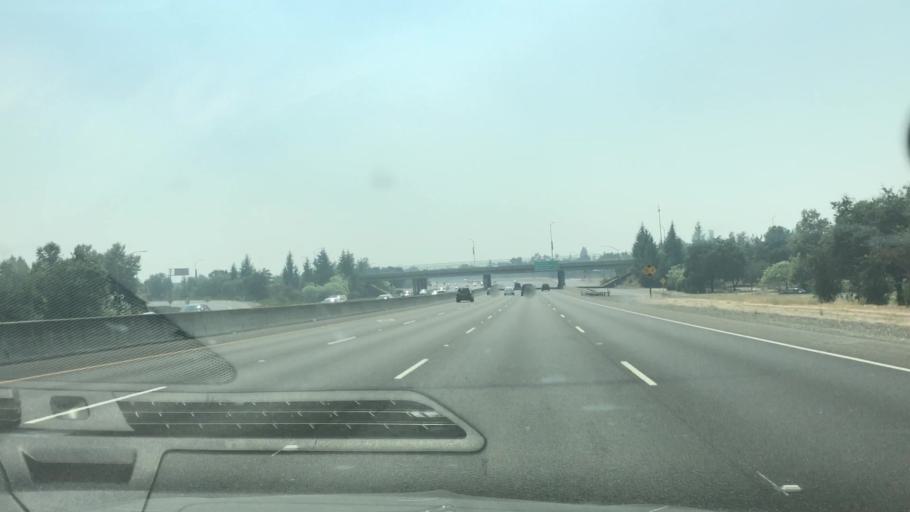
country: US
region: California
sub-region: Sacramento County
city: Gold River
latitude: 38.6106
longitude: -121.2678
